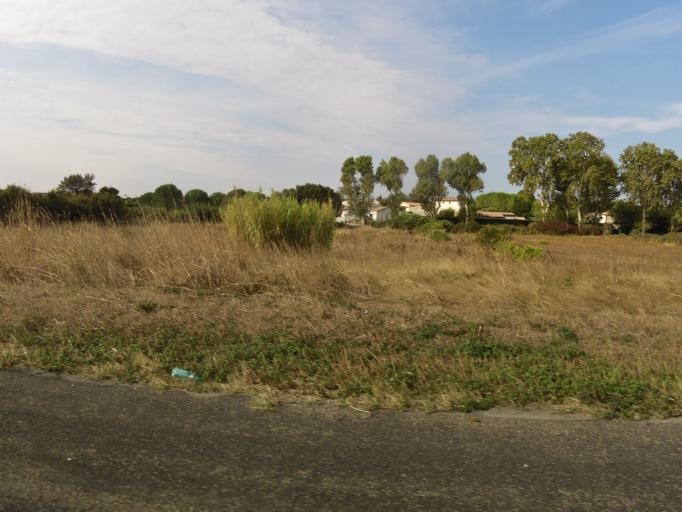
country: FR
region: Languedoc-Roussillon
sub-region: Departement de l'Herault
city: Boisseron
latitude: 43.7529
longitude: 4.0898
